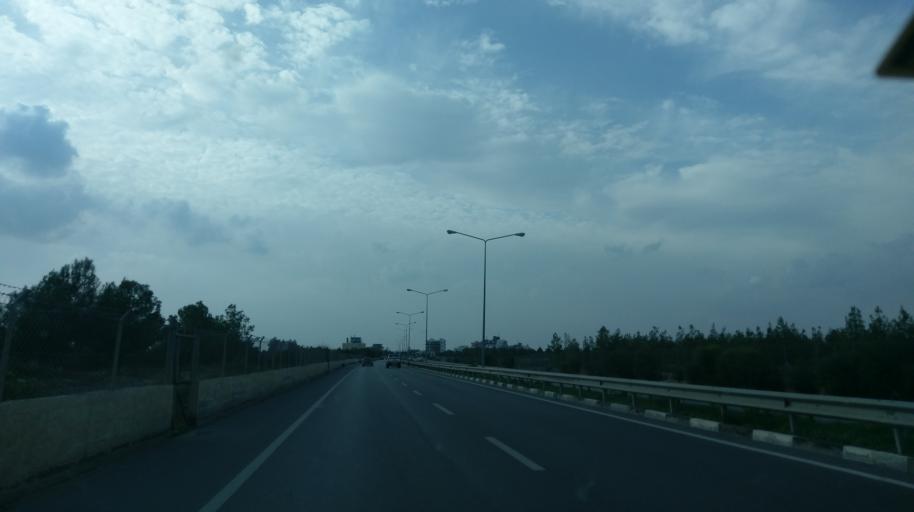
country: CY
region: Lefkosia
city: Nicosia
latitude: 35.1898
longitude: 33.3339
